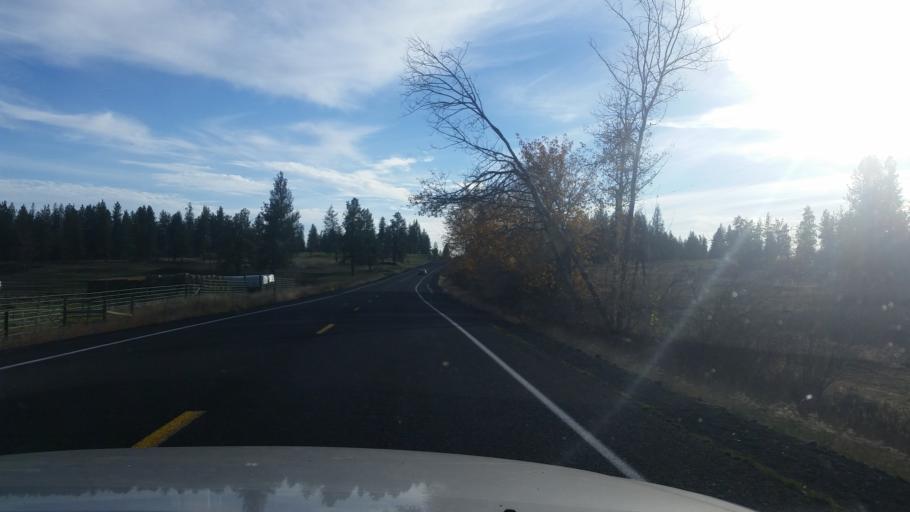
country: US
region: Washington
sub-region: Spokane County
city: Cheney
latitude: 47.3725
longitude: -117.5873
